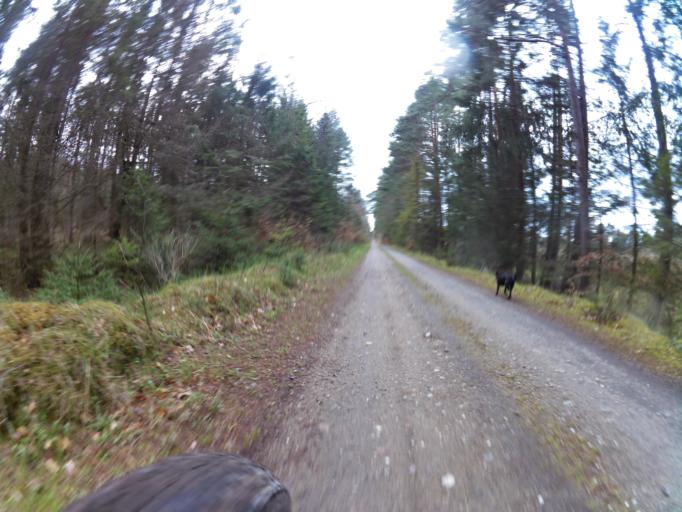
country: PL
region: West Pomeranian Voivodeship
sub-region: Powiat slawienski
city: Slawno
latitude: 54.3199
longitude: 16.7796
